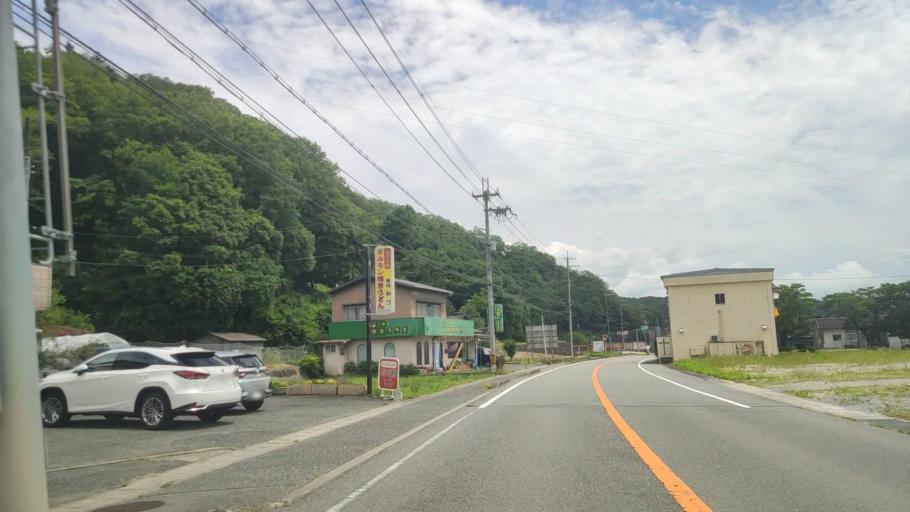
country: JP
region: Hyogo
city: Yamazakicho-nakabirose
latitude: 35.0263
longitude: 134.3708
